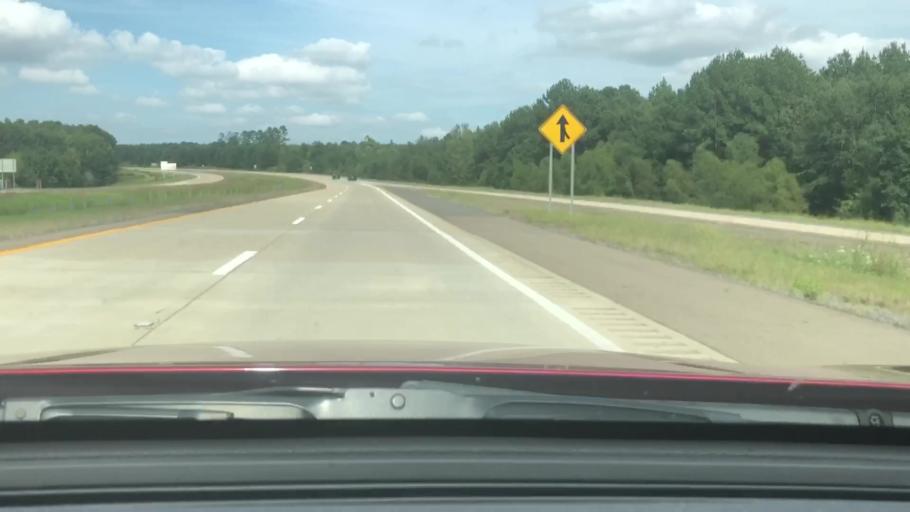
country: US
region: Louisiana
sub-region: Caddo Parish
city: Vivian
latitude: 33.0820
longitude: -93.8980
